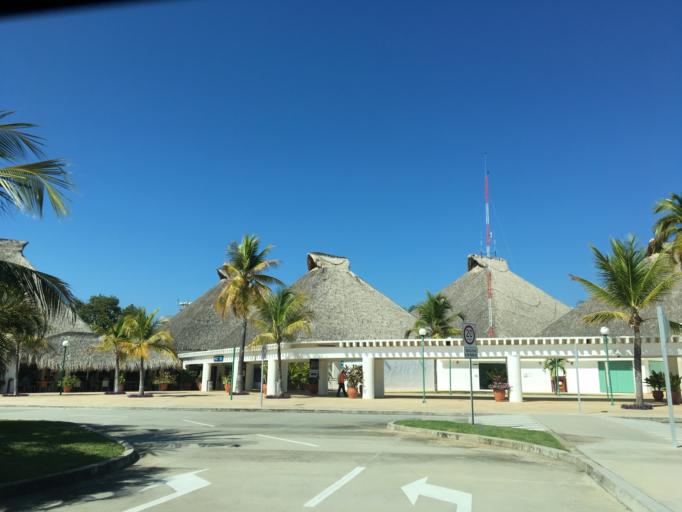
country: MX
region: Oaxaca
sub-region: Santa Maria Huatulco
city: Cuapinolito (Azulillo)
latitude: 15.7715
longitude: -96.2586
